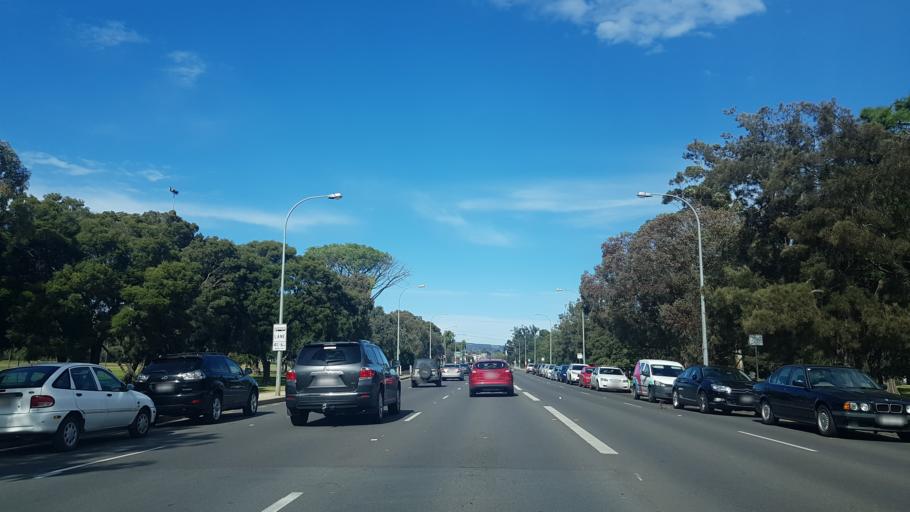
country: AU
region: South Australia
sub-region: Unley
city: Wayville
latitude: -34.9385
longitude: 138.5887
